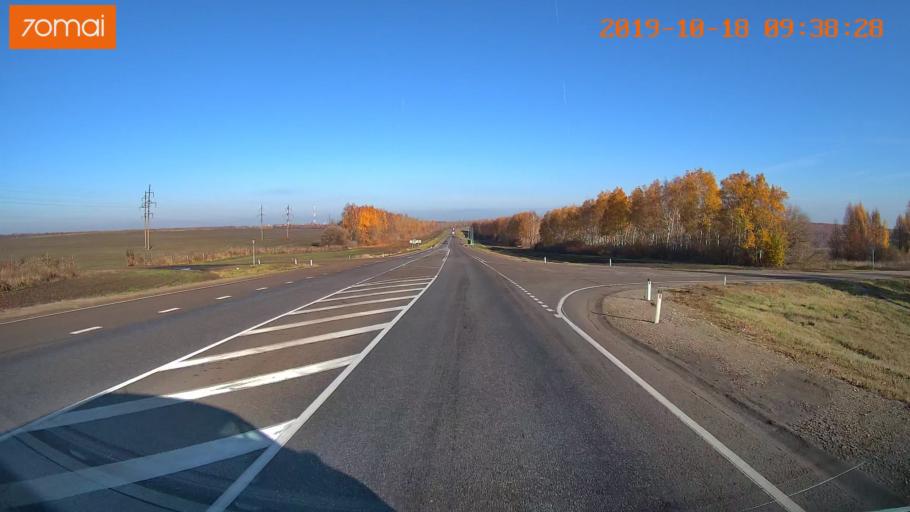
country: RU
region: Tula
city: Yefremov
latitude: 53.2385
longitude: 38.1370
